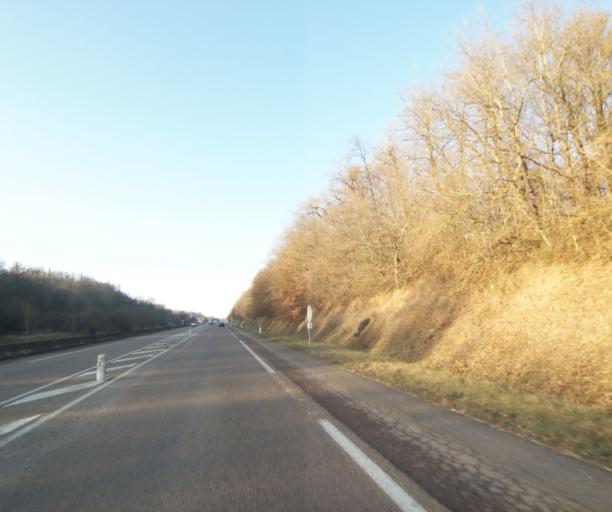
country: FR
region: Champagne-Ardenne
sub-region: Departement de la Haute-Marne
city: Chevillon
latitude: 48.5023
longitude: 5.1044
